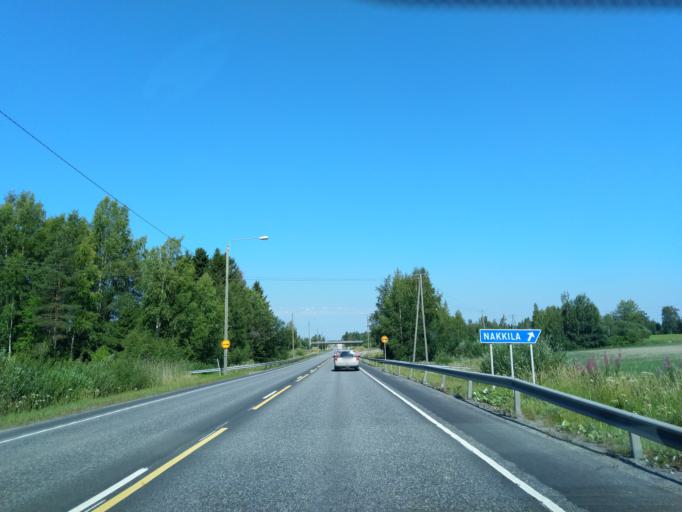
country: FI
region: Satakunta
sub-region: Pori
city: Nakkila
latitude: 61.3587
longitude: 22.0000
